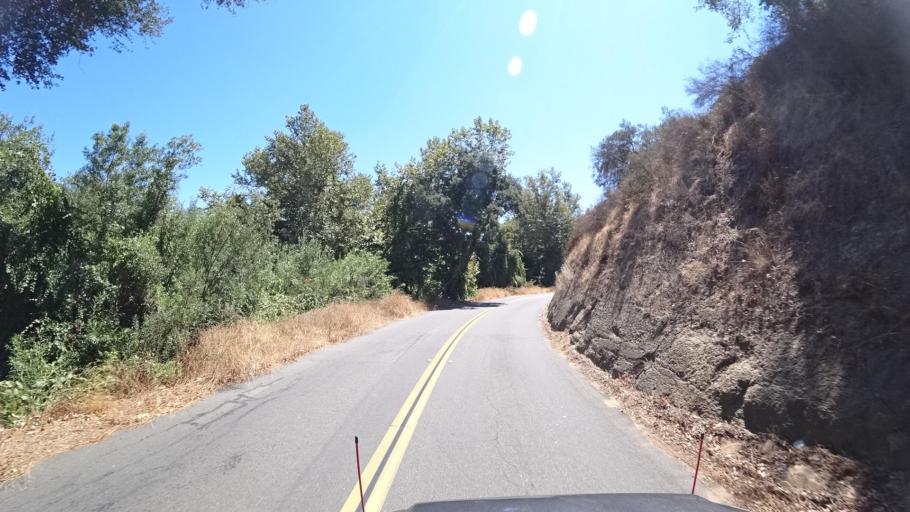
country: US
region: California
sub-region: San Diego County
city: Rainbow
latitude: 33.3240
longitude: -117.1041
